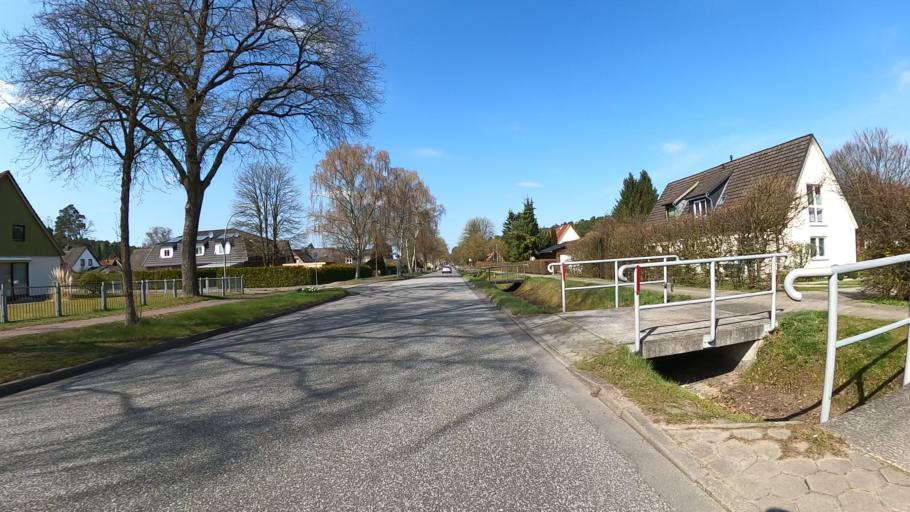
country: DE
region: Lower Saxony
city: Neu Wulmstorf
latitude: 53.4551
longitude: 9.8669
